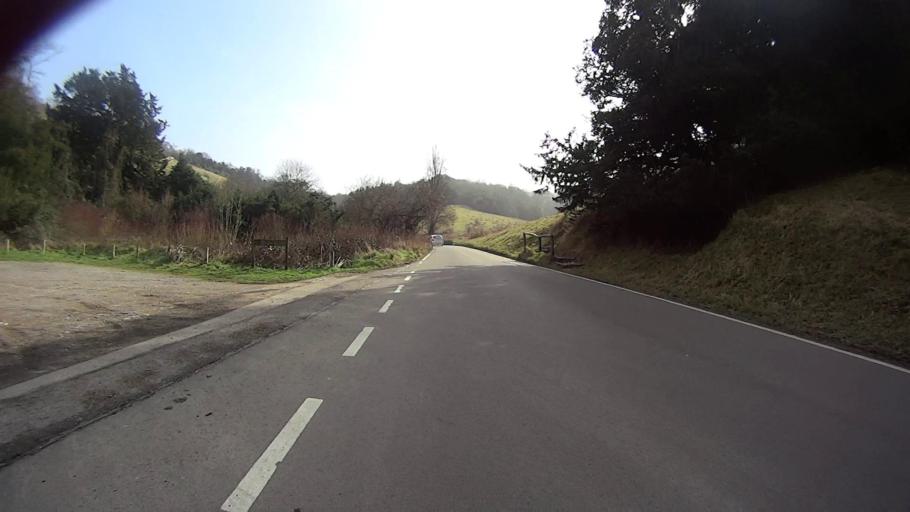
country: GB
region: England
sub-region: Surrey
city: Mickleham
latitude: 51.2546
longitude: -0.3153
